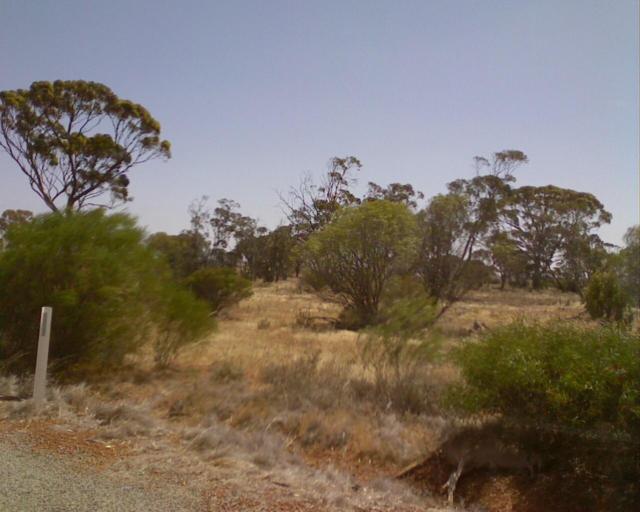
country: AU
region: Western Australia
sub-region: Merredin
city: Merredin
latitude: -30.8126
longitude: 118.2096
